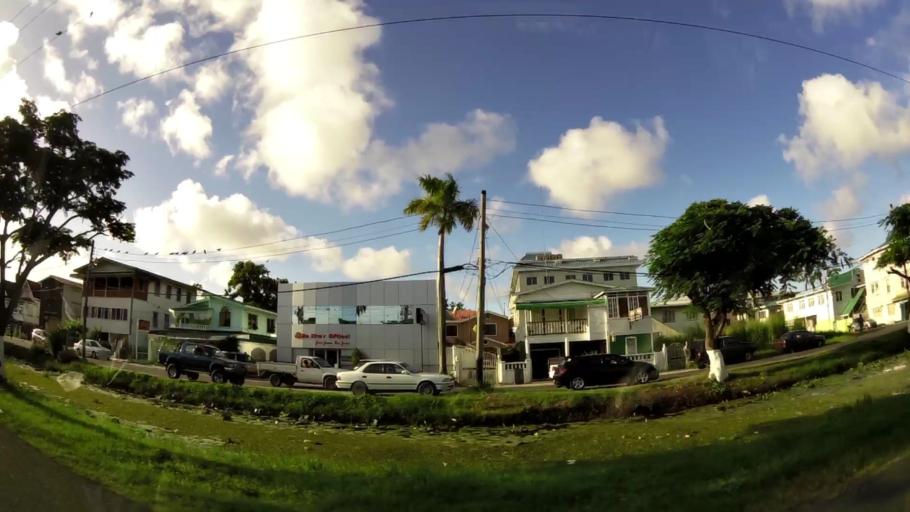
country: GY
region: Demerara-Mahaica
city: Georgetown
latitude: 6.8064
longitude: -58.1532
